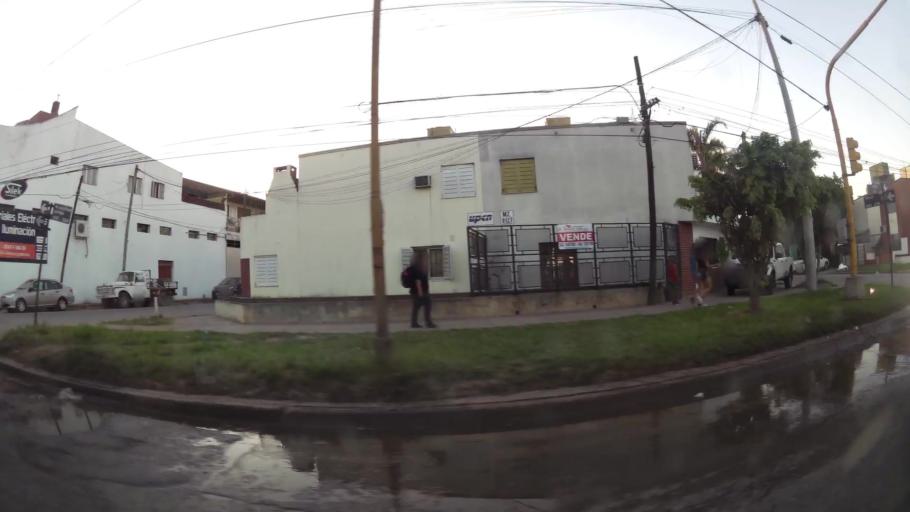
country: AR
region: Santa Fe
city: Santa Fe de la Vera Cruz
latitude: -31.5926
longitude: -60.6921
